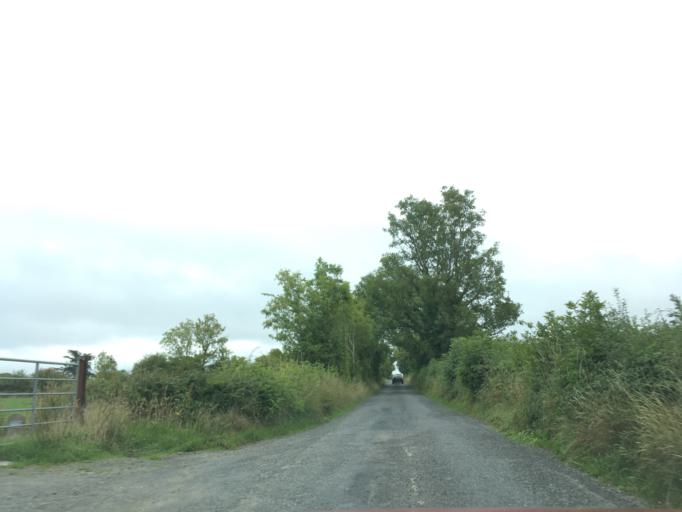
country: IE
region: Munster
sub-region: An Clar
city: Ennis
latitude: 52.7192
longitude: -9.0816
